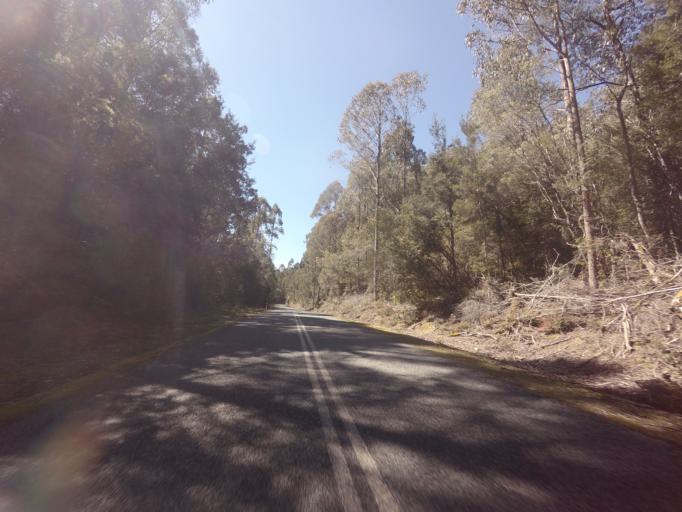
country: AU
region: Tasmania
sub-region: Huon Valley
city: Geeveston
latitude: -42.7896
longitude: 146.3983
